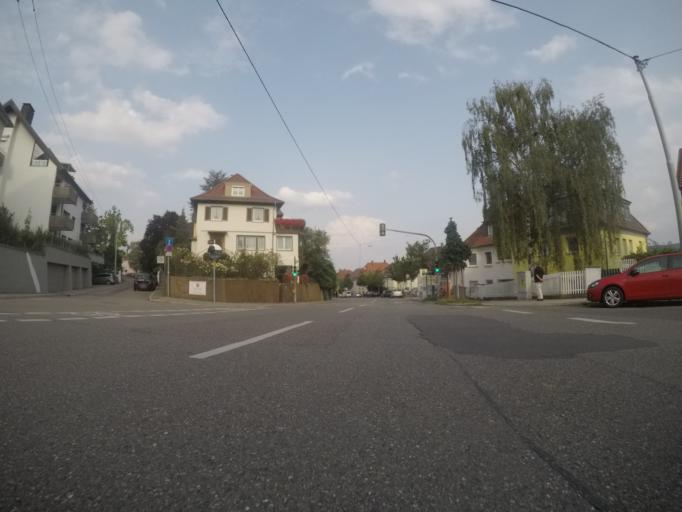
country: DE
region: Baden-Wuerttemberg
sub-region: Regierungsbezirk Stuttgart
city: Stuttgart
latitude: 48.7794
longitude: 9.1513
